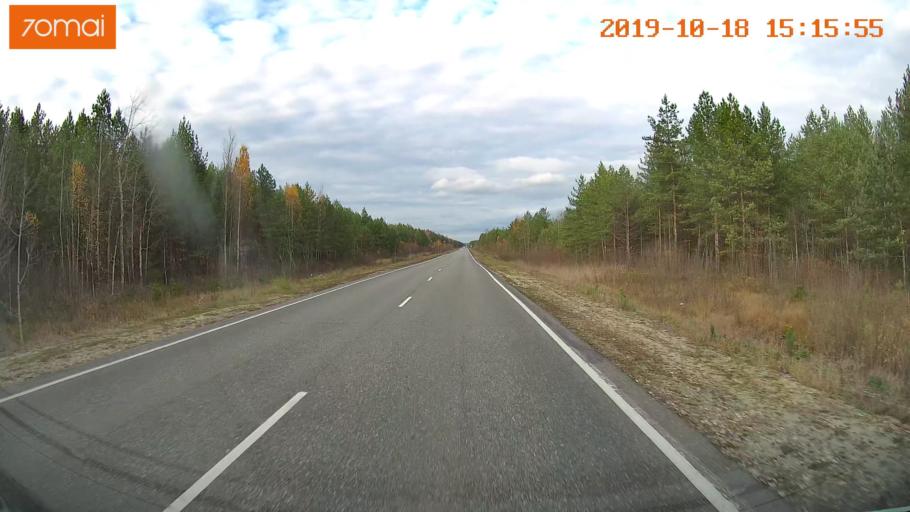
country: RU
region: Vladimir
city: Gus'-Khrustal'nyy
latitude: 55.6271
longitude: 40.7236
